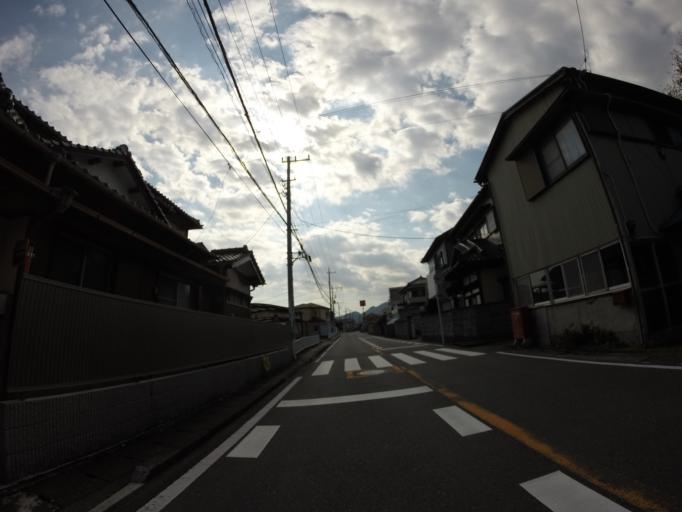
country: JP
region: Shizuoka
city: Fujinomiya
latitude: 35.1754
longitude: 138.6358
